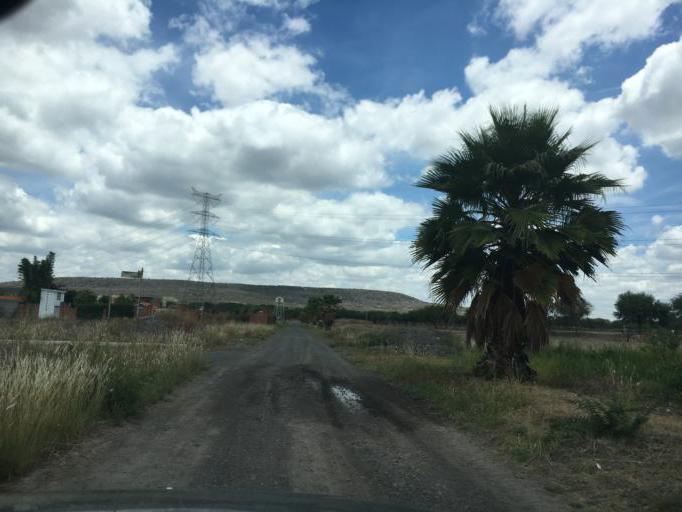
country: MX
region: Guanajuato
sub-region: Leon
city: Plan Guanajuato (La Sandia)
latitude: 20.9255
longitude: -101.7499
